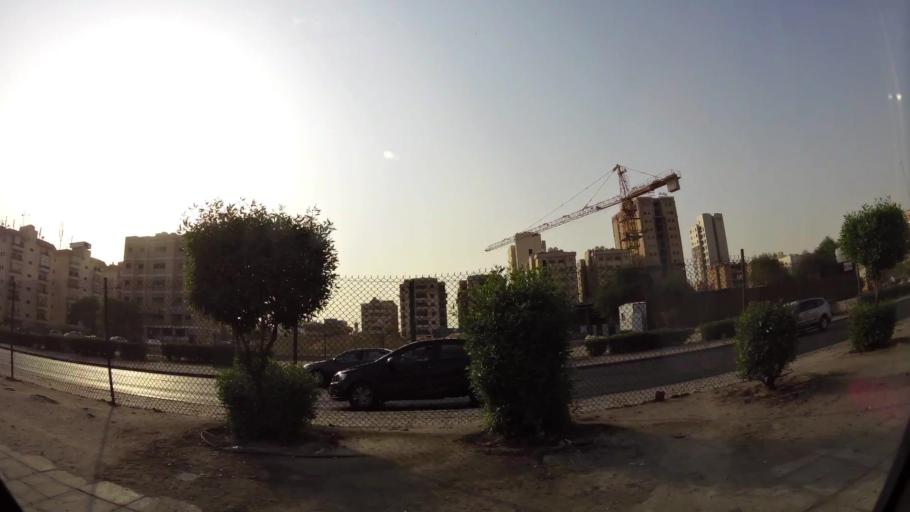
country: KW
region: Muhafazat Hawalli
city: Hawalli
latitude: 29.3256
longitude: 48.0212
